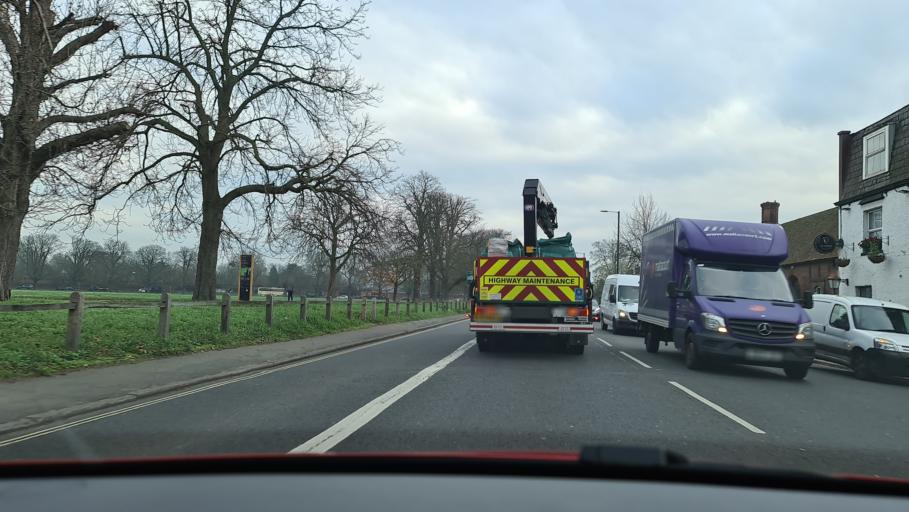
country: GB
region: England
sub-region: Surrey
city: East Molesey
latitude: 51.4066
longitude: -0.3443
